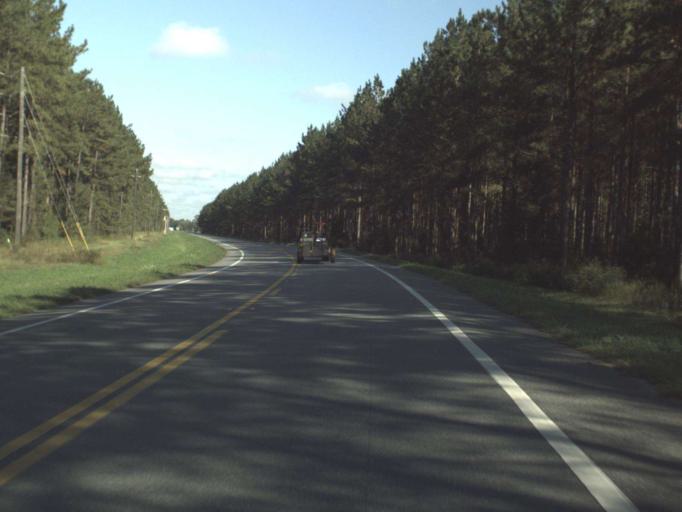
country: US
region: Florida
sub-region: Gulf County
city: Wewahitchka
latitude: 30.2275
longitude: -85.2047
